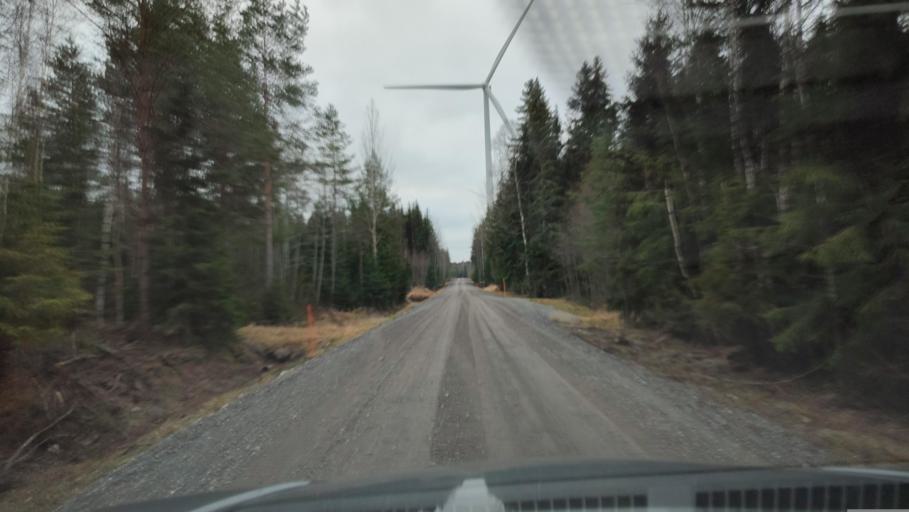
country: FI
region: Southern Ostrobothnia
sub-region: Suupohja
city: Karijoki
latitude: 62.2130
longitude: 21.6020
